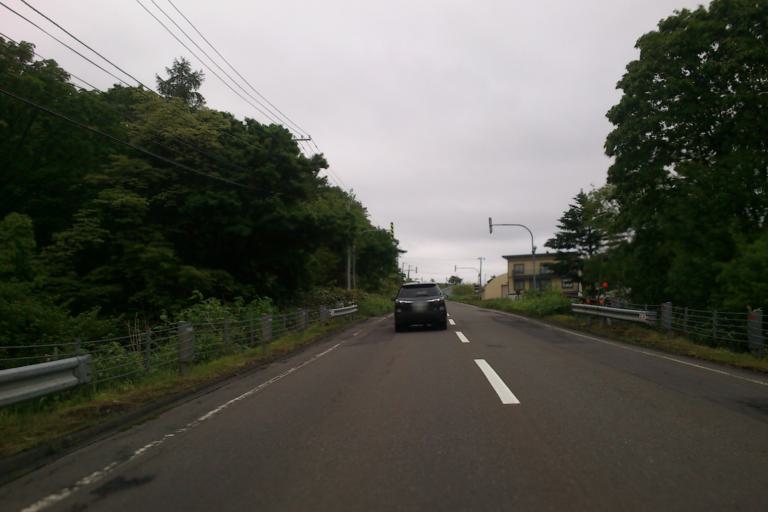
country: JP
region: Hokkaido
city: Ishikari
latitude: 43.3274
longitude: 141.4424
